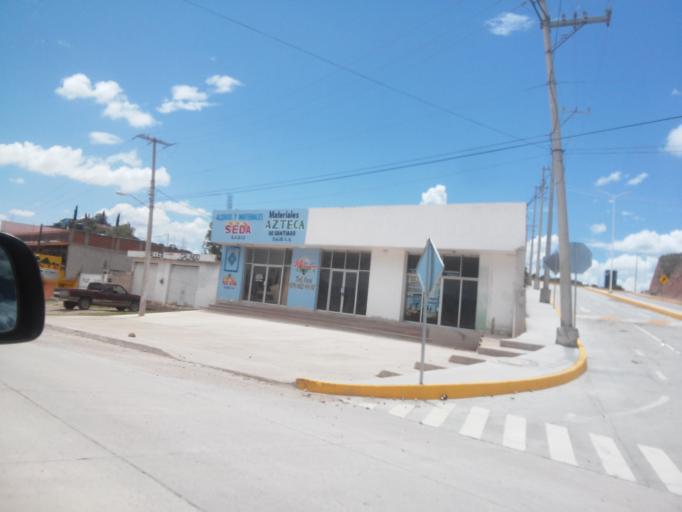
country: MX
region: Durango
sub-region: Santiago Papasquiaro
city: Santiago Papasquiaro
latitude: 25.0588
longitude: -105.4259
